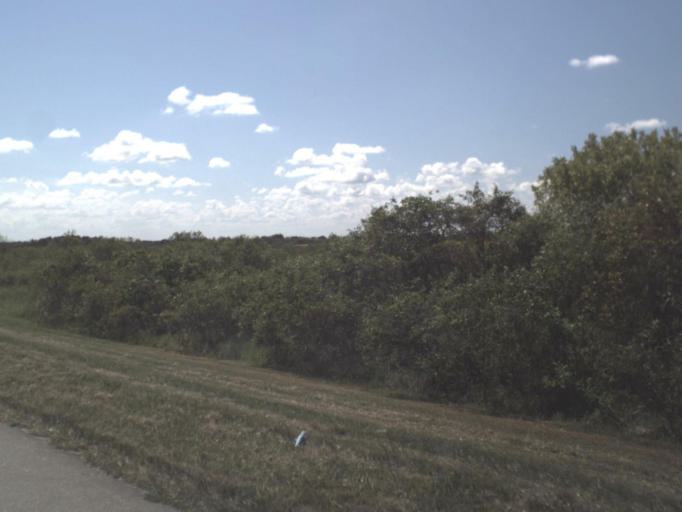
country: US
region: Florida
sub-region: Glades County
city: Moore Haven
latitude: 26.9651
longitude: -81.1201
